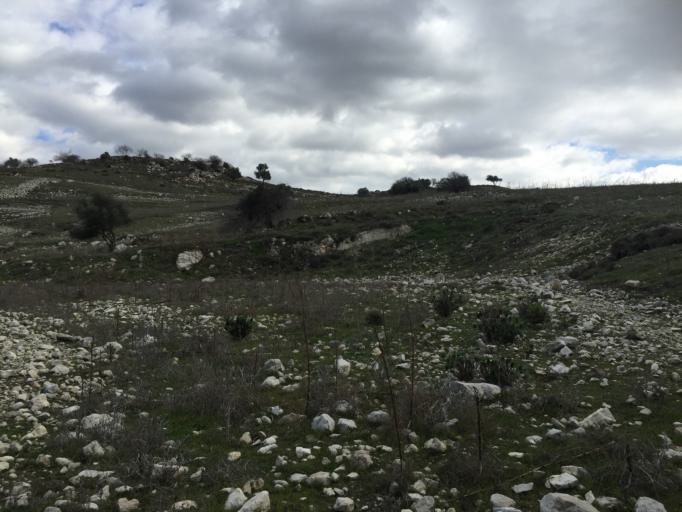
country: CY
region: Pafos
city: Pegeia
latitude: 34.9231
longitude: 32.3649
